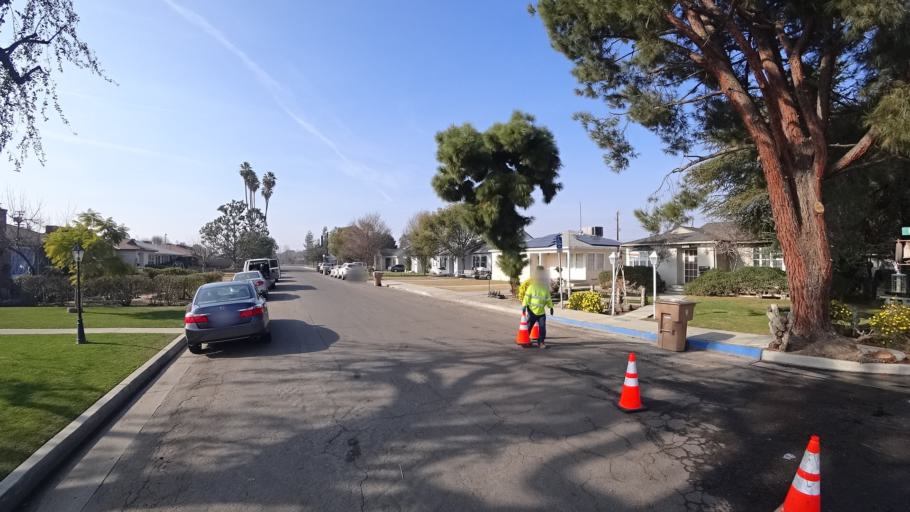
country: US
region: California
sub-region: Kern County
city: Bakersfield
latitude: 35.3591
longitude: -119.0374
